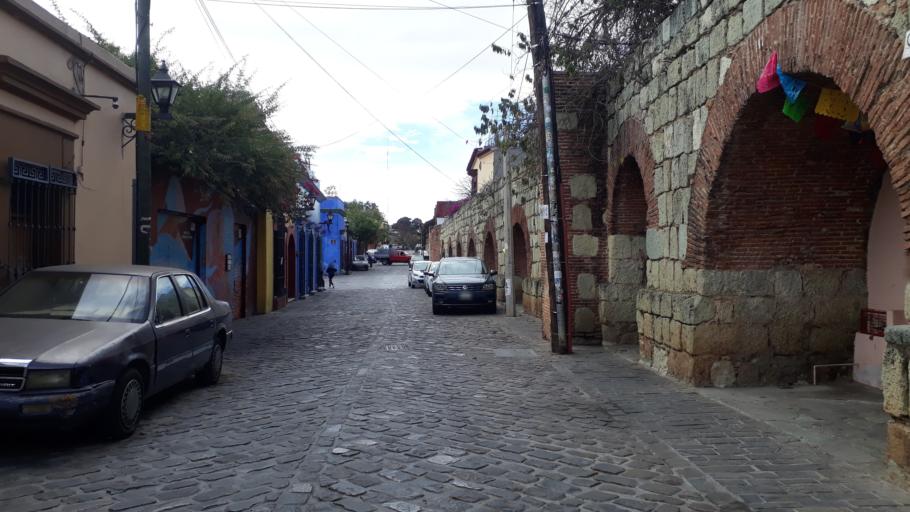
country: MX
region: Oaxaca
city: Oaxaca de Juarez
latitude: 17.0702
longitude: -96.7241
